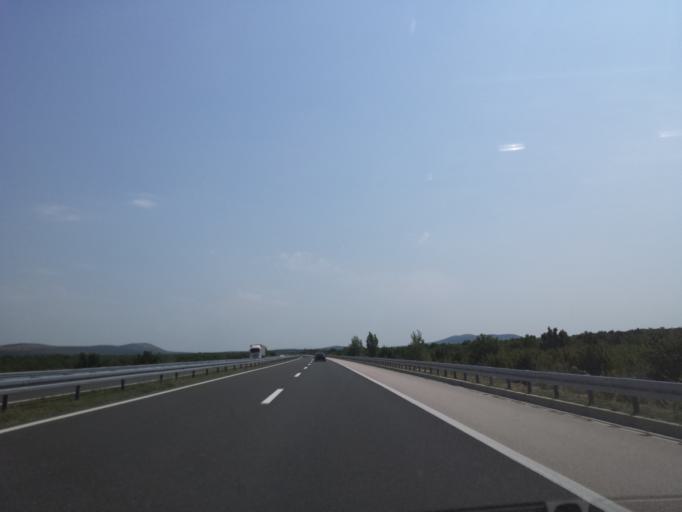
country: HR
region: Zadarska
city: Benkovac
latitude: 43.9682
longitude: 15.6517
